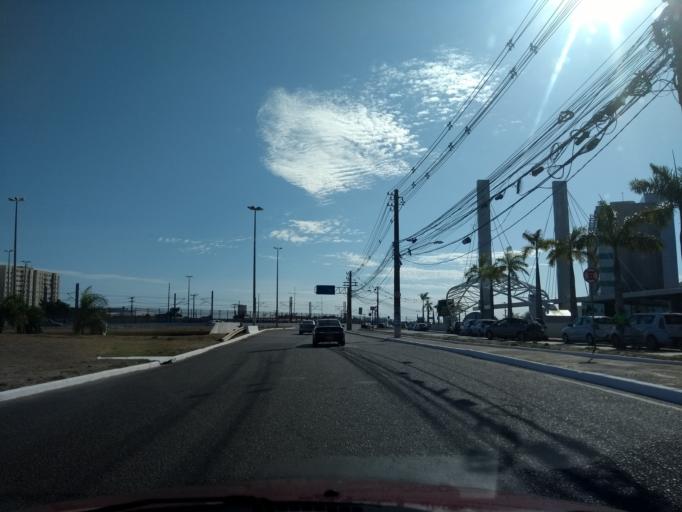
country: BR
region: Bahia
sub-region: Lauro De Freitas
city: Lauro de Freitas
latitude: -12.9198
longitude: -38.3543
